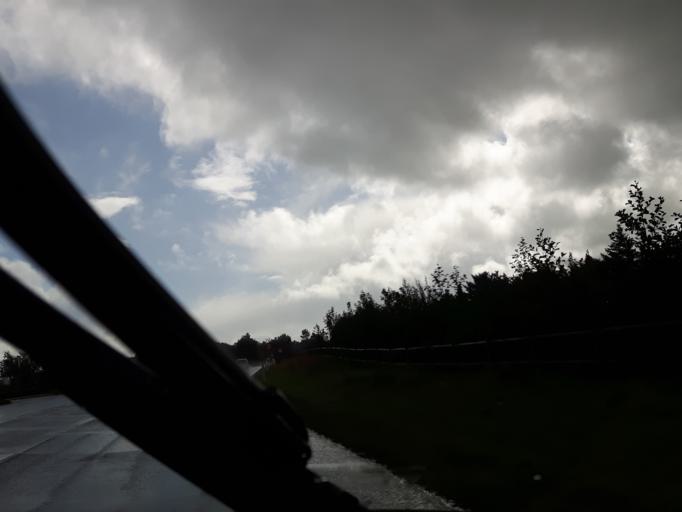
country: DK
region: Central Jutland
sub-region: Struer Kommune
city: Struer
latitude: 56.6074
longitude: 8.5301
